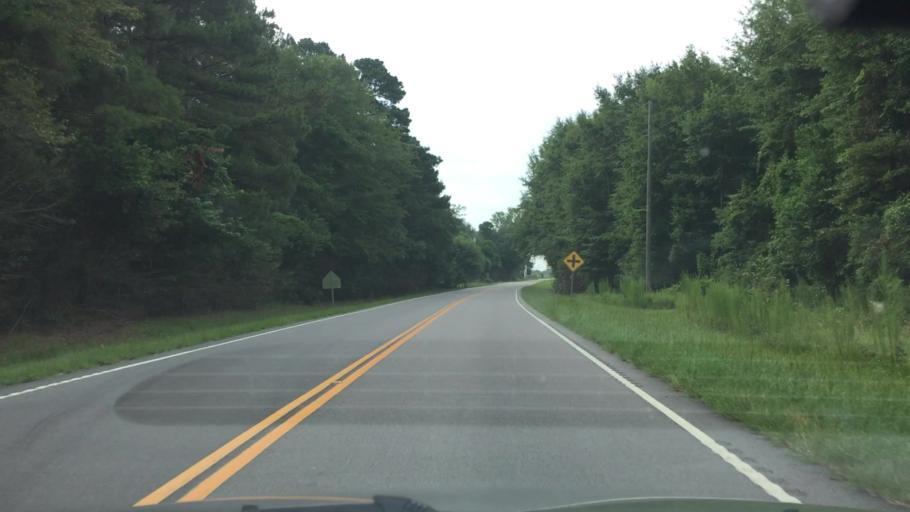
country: US
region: South Carolina
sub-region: Lexington County
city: Batesburg-Leesville
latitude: 33.7033
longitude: -81.4829
